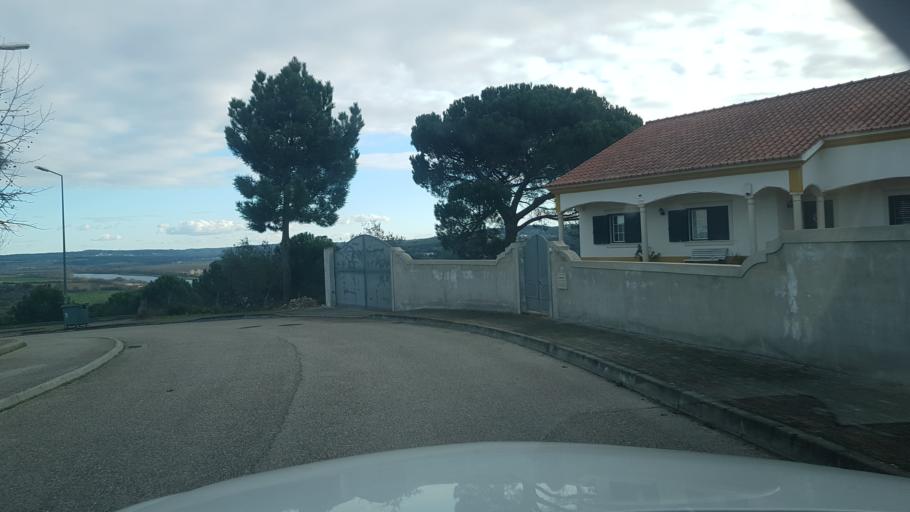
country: PT
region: Santarem
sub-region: Constancia
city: Constancia
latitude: 39.4824
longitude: -8.3309
